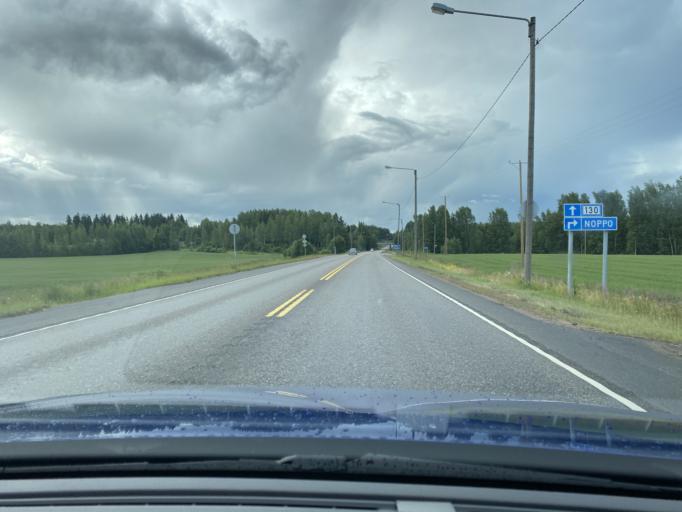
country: FI
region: Uusimaa
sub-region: Helsinki
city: Hyvinge
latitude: 60.5672
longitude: 24.8098
